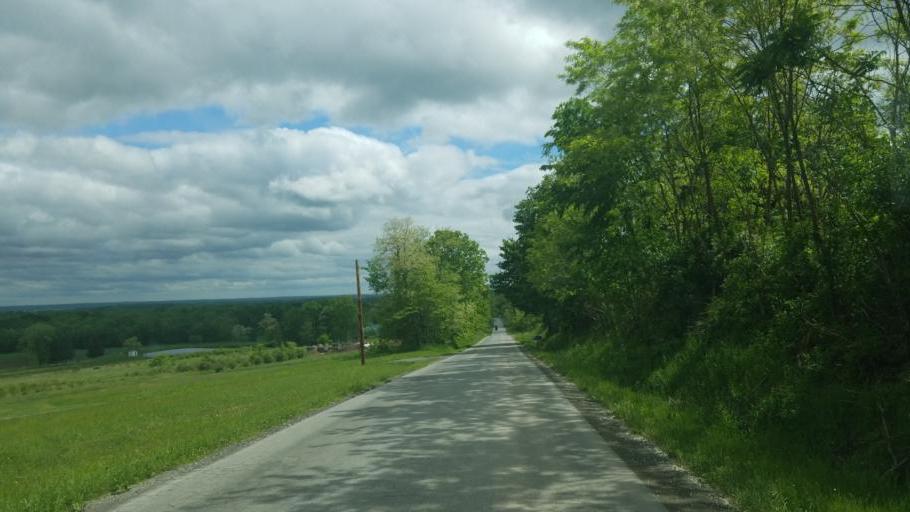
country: US
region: Ohio
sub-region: Geauga County
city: Middlefield
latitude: 41.4331
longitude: -81.0033
